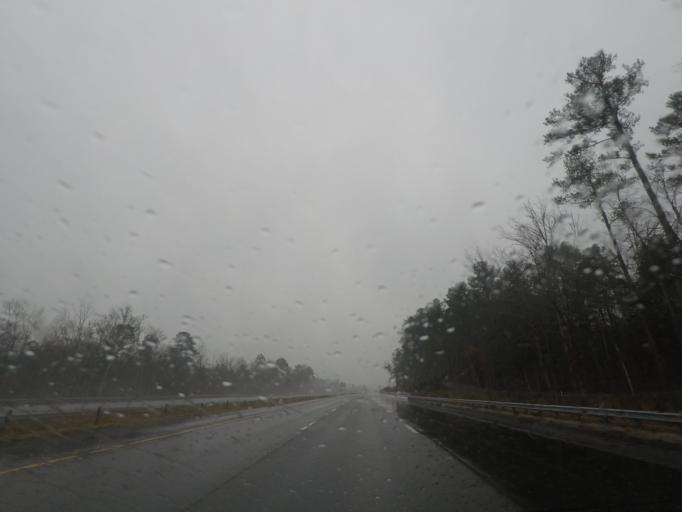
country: US
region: North Carolina
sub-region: Wake County
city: Morrisville
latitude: 35.8878
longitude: -78.8715
